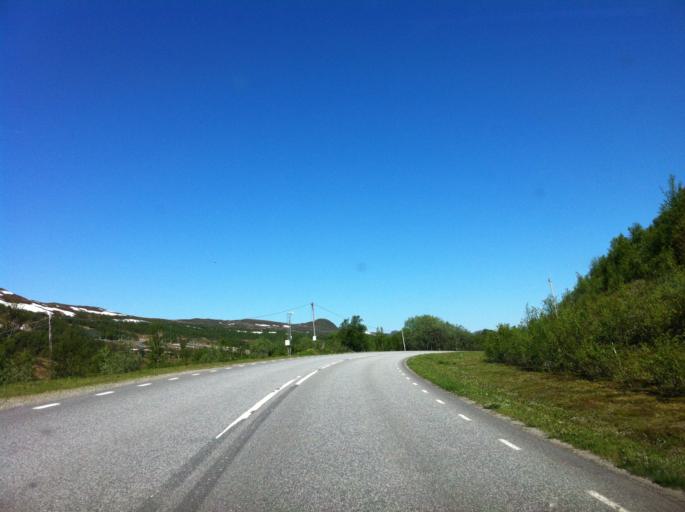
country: NO
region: Sor-Trondelag
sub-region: Tydal
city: Aas
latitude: 62.5563
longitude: 12.2743
